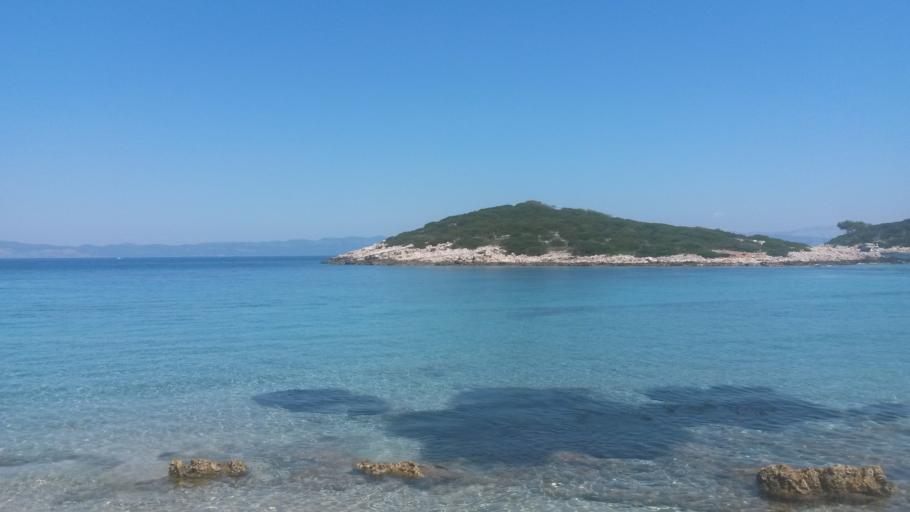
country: HR
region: Dubrovacko-Neretvanska
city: Smokvica
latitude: 42.7794
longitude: 16.9860
